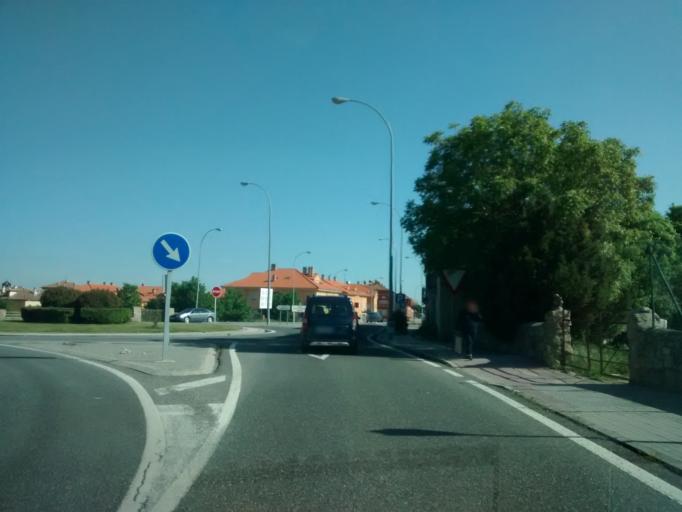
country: ES
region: Castille and Leon
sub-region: Provincia de Segovia
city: Torrecaballeros
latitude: 40.9937
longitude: -4.0221
